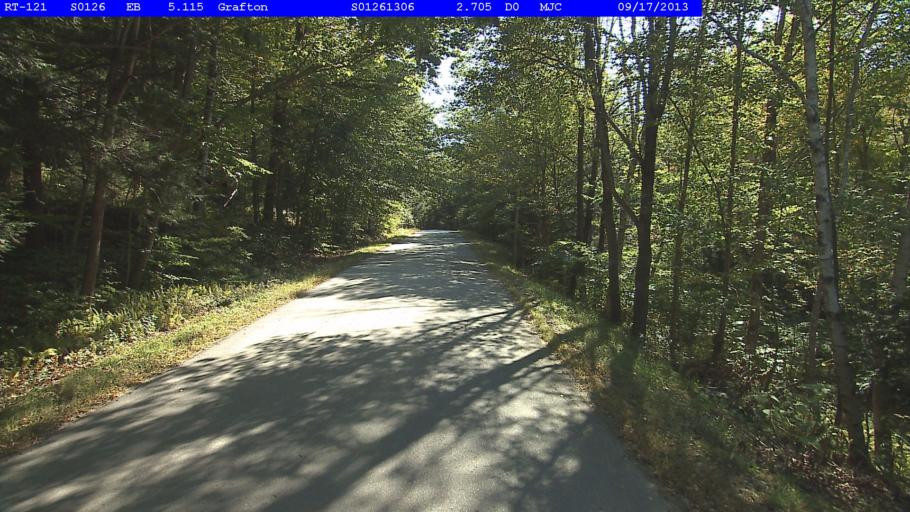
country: US
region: Vermont
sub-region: Windsor County
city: Chester
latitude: 43.1973
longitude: -72.6360
